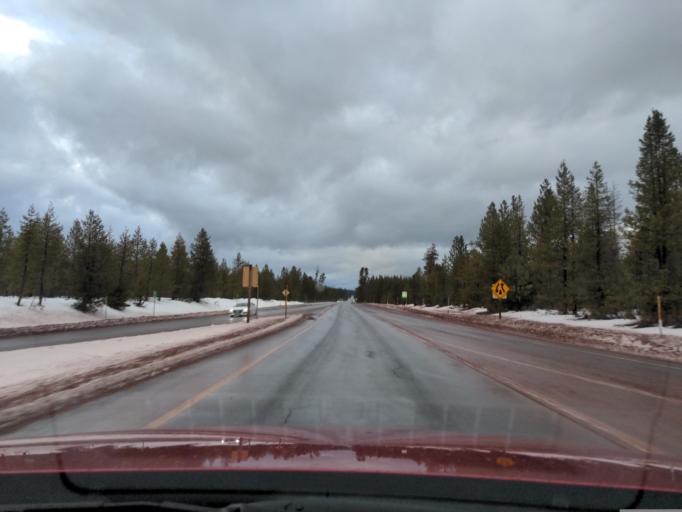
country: US
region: Oregon
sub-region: Deschutes County
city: La Pine
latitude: 43.3325
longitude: -121.7581
